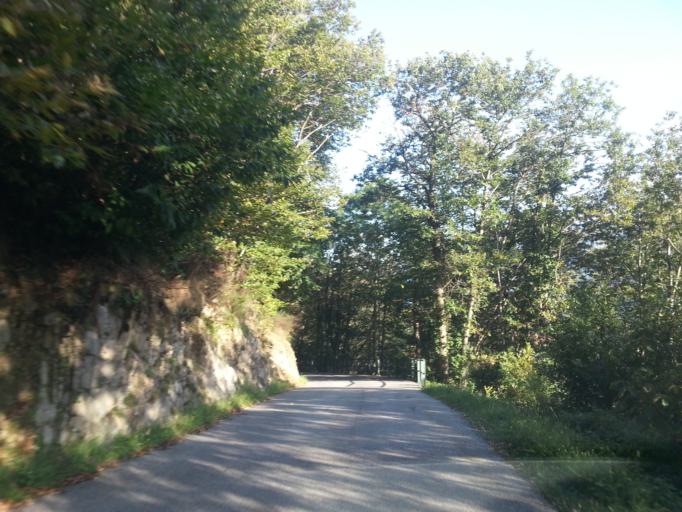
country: IT
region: Lombardy
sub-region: Provincia di Como
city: Sorico
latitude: 46.1831
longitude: 9.3869
